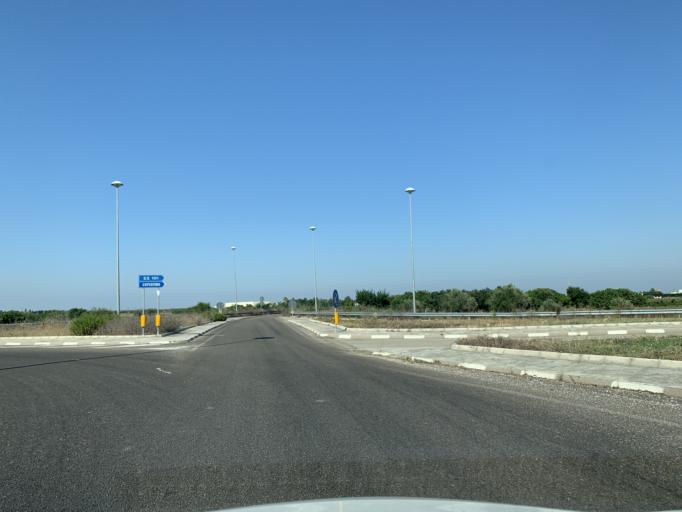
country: IT
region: Apulia
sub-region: Provincia di Lecce
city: Nardo
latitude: 40.1884
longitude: 18.0325
